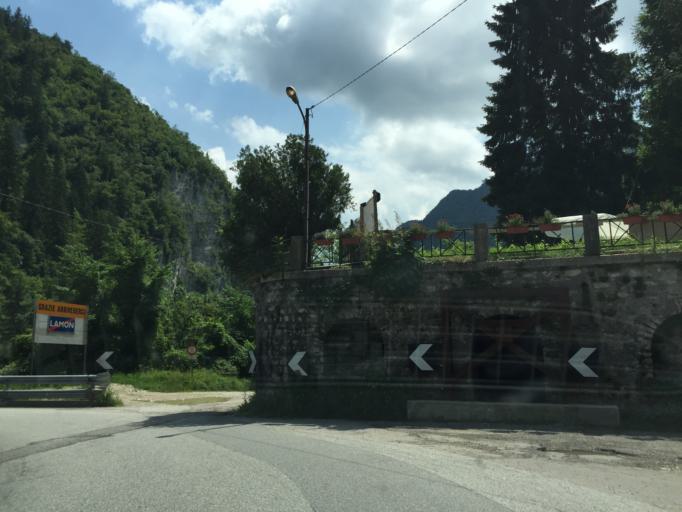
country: IT
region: Veneto
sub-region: Provincia di Belluno
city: Lamon
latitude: 46.0298
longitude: 11.7627
